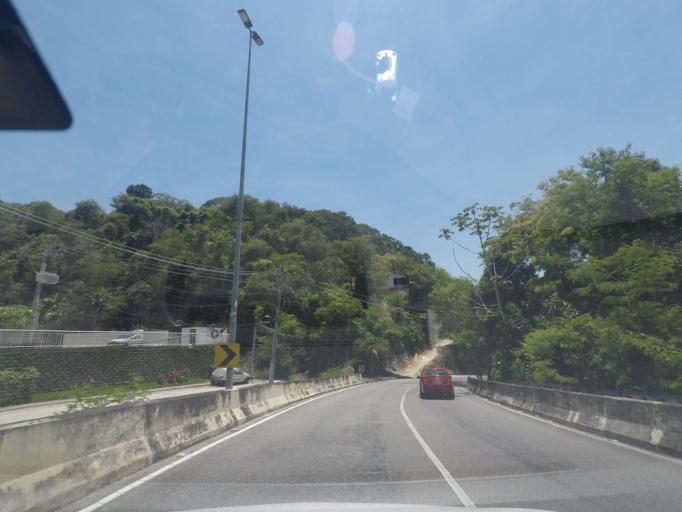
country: BR
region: Rio de Janeiro
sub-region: Niteroi
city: Niteroi
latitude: -22.9202
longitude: -43.0637
